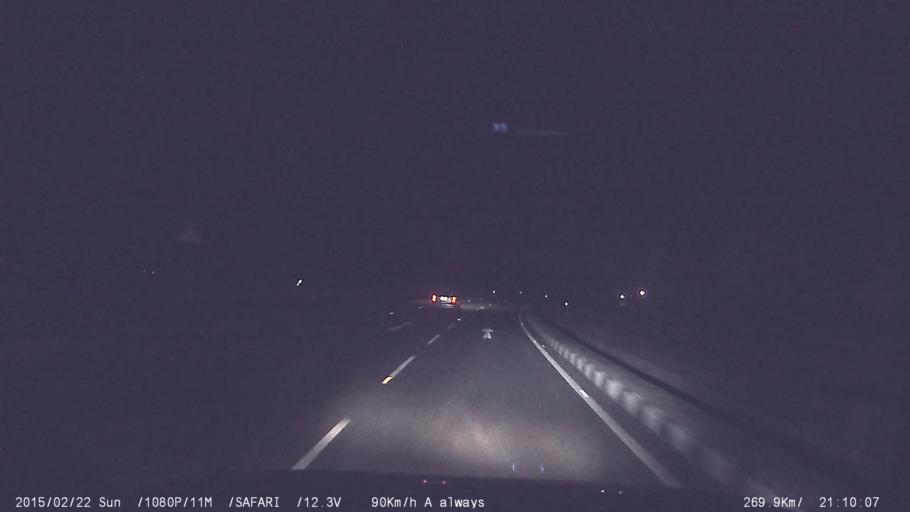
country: IN
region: Tamil Nadu
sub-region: Karur
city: Pallappatti
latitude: 10.7551
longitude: 77.9120
